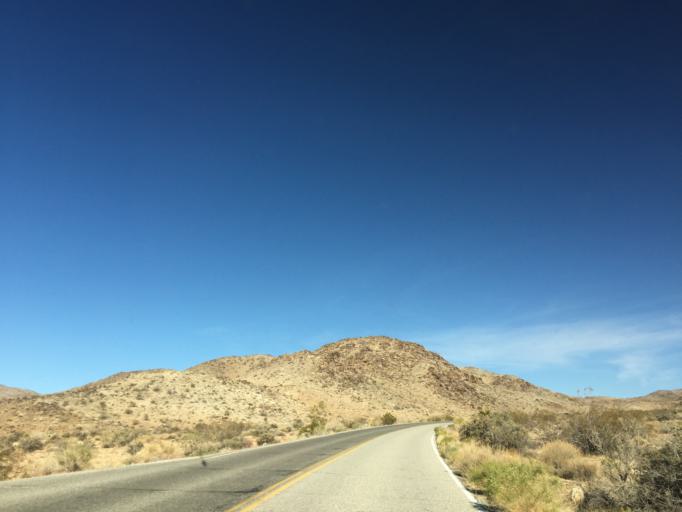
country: US
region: California
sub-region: San Bernardino County
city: Twentynine Palms
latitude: 33.9478
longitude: -115.9789
